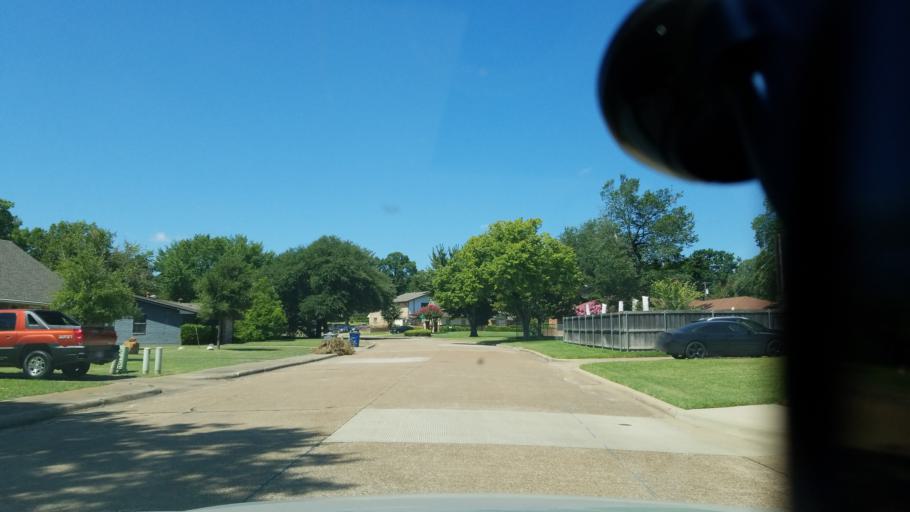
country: US
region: Texas
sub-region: Dallas County
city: Cockrell Hill
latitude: 32.6781
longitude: -96.8343
